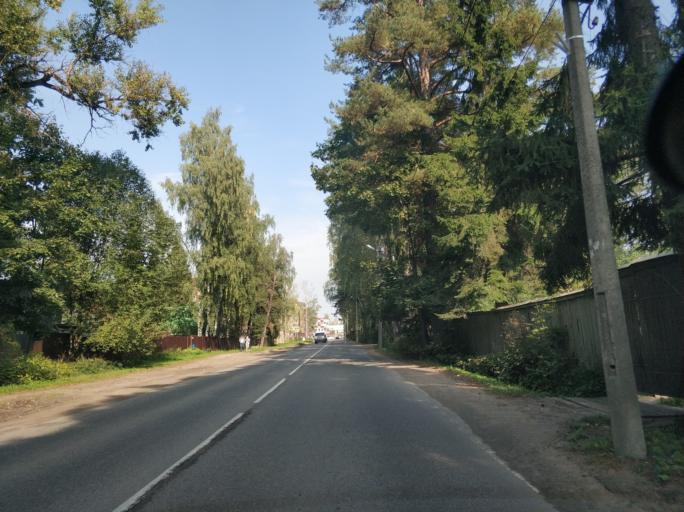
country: RU
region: Leningrad
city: Vsevolozhsk
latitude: 60.0144
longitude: 30.6222
